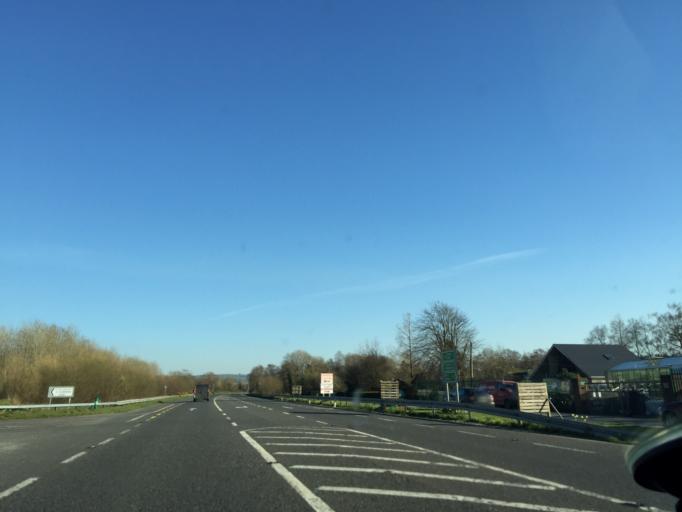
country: IE
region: Munster
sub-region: Ciarrai
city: Castleisland
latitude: 52.1935
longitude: -9.5666
